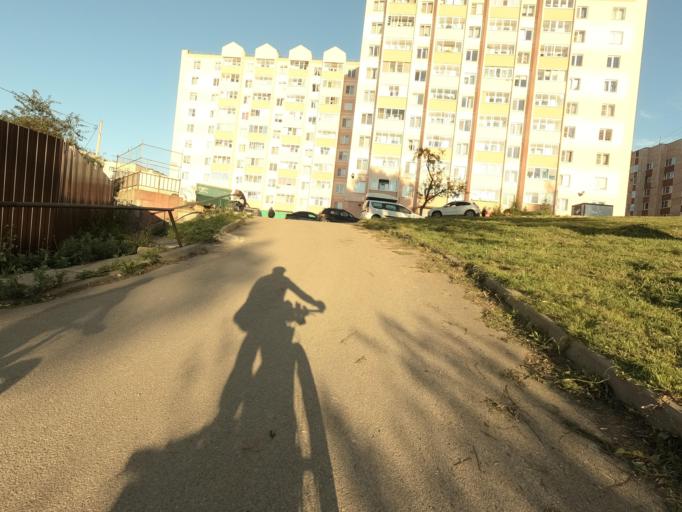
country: RU
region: Leningrad
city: Nikol'skoye
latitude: 59.7079
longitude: 30.7746
